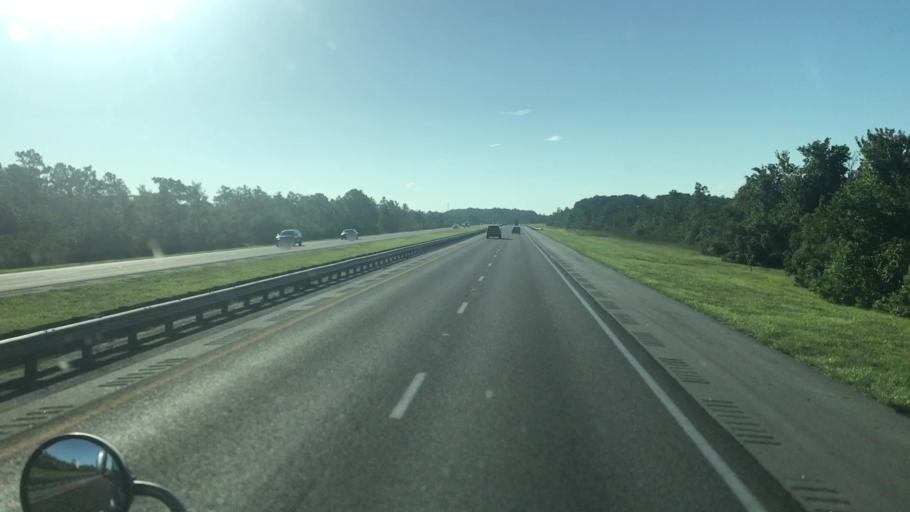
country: US
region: Florida
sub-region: Osceola County
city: Saint Cloud
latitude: 28.0053
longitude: -81.1509
